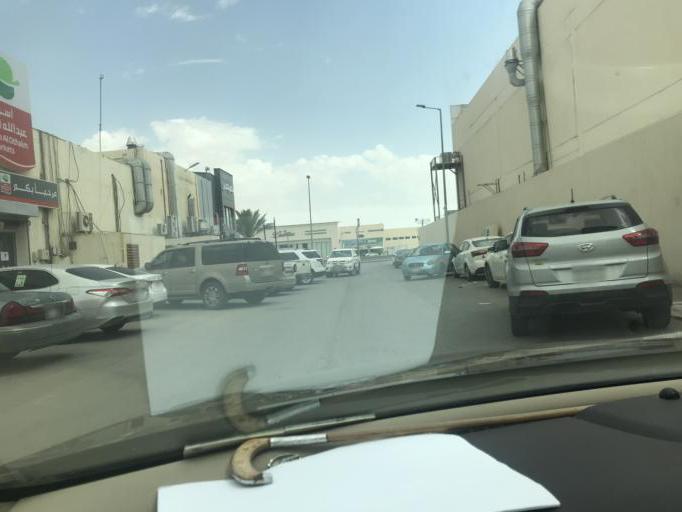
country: SA
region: Ar Riyad
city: Riyadh
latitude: 24.7286
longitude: 46.7821
